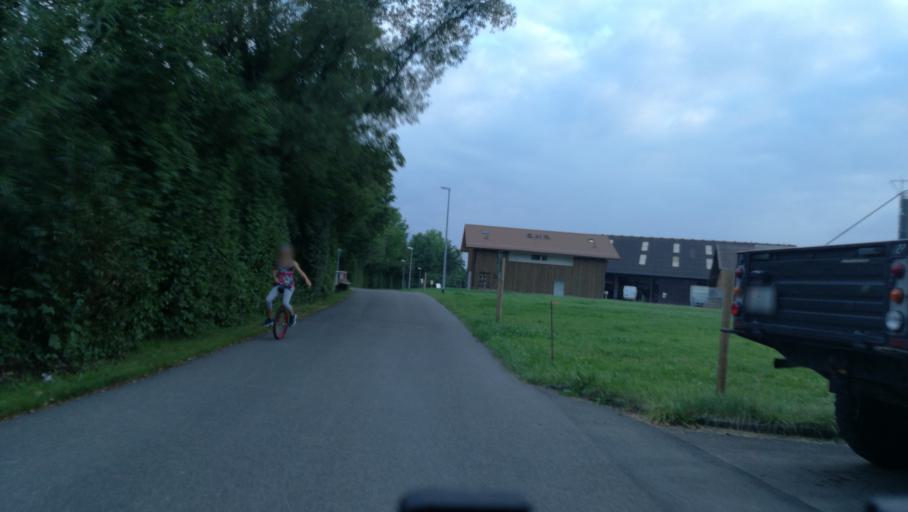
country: CH
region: Zug
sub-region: Zug
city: Zug
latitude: 47.1814
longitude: 8.5019
